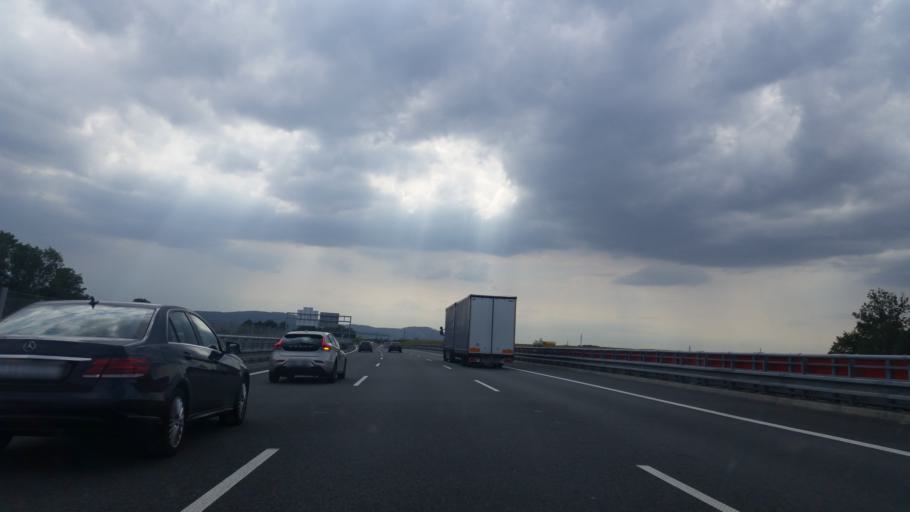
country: CZ
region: Olomoucky
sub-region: Okres Prerov
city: Hranice
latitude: 49.5828
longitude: 17.7510
